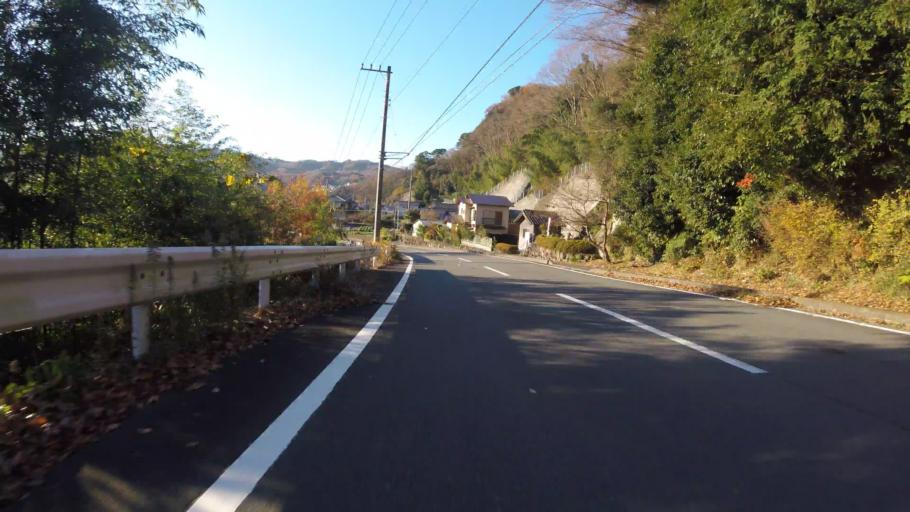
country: JP
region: Shizuoka
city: Mishima
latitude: 34.9984
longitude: 138.9310
